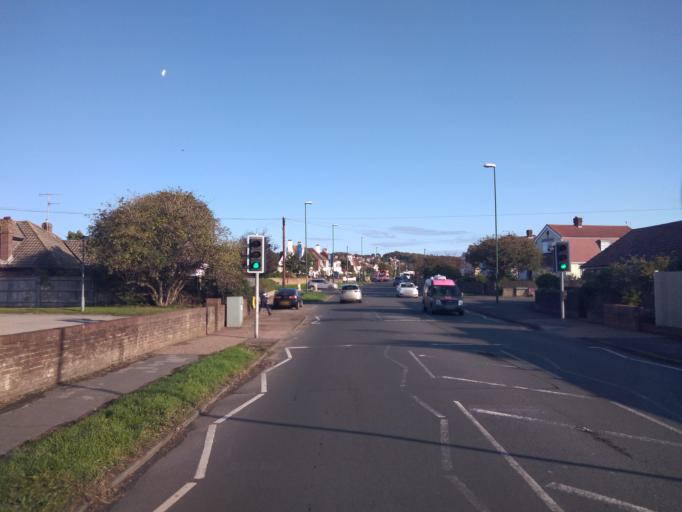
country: GB
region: England
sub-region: West Sussex
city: Lancing
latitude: 50.8313
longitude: -0.3187
